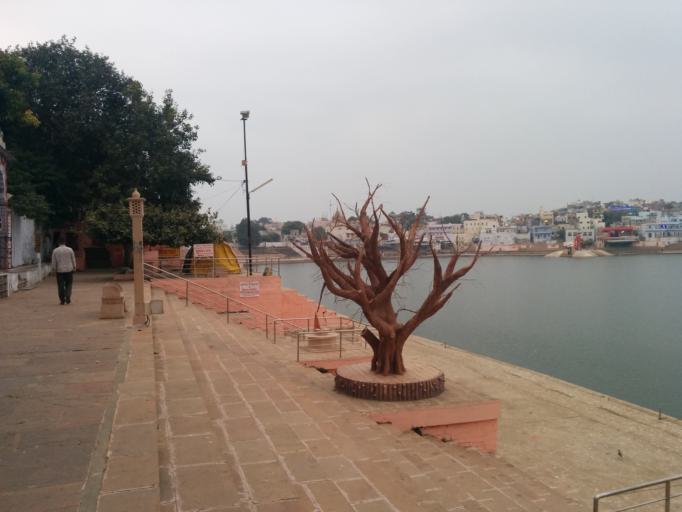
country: IN
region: Rajasthan
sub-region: Ajmer
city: Pushkar
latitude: 26.4861
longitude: 74.5548
